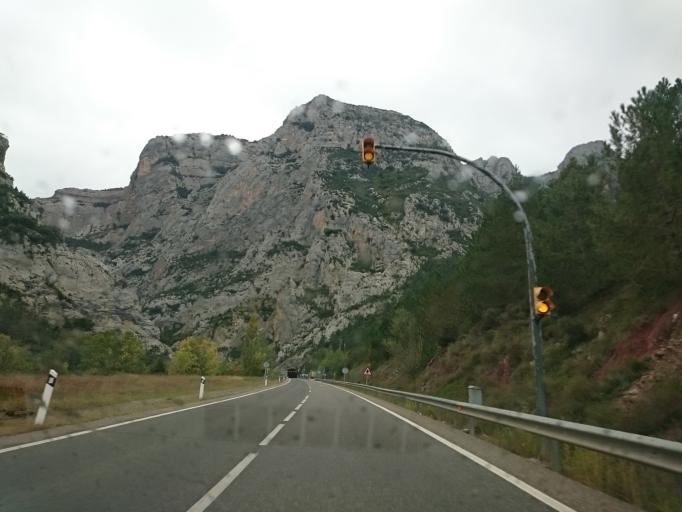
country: ES
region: Catalonia
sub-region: Provincia de Lleida
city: Senterada
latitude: 42.3014
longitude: 1.0376
